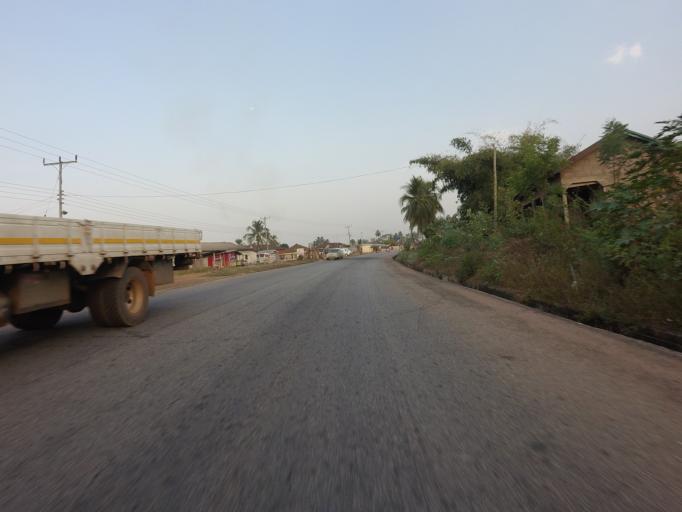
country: GH
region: Volta
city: Ho
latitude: 6.5742
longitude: 0.3791
